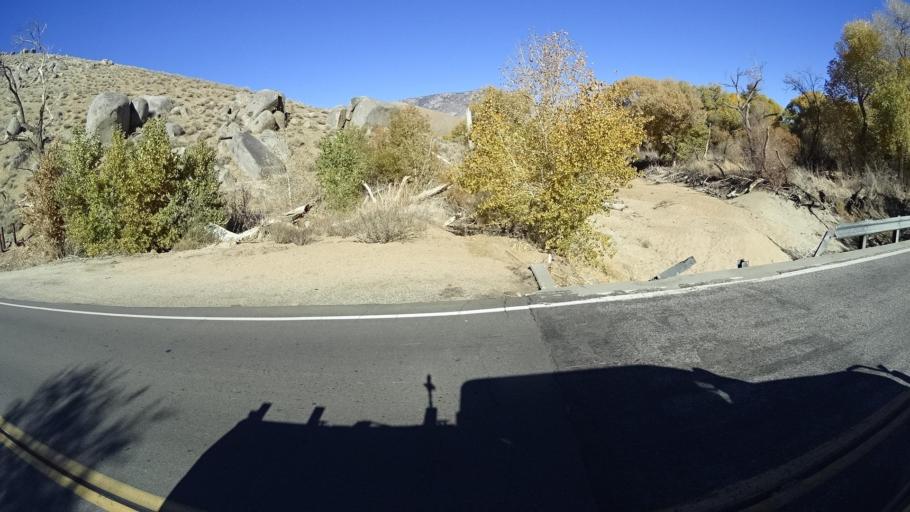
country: US
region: California
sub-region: Kern County
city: Weldon
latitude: 35.6726
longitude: -118.3277
